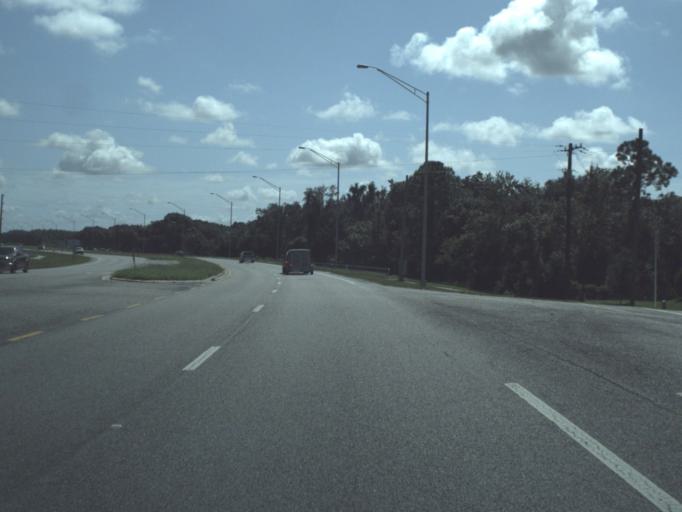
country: US
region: Florida
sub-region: Sarasota County
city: The Meadows
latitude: 27.4761
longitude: -82.4004
